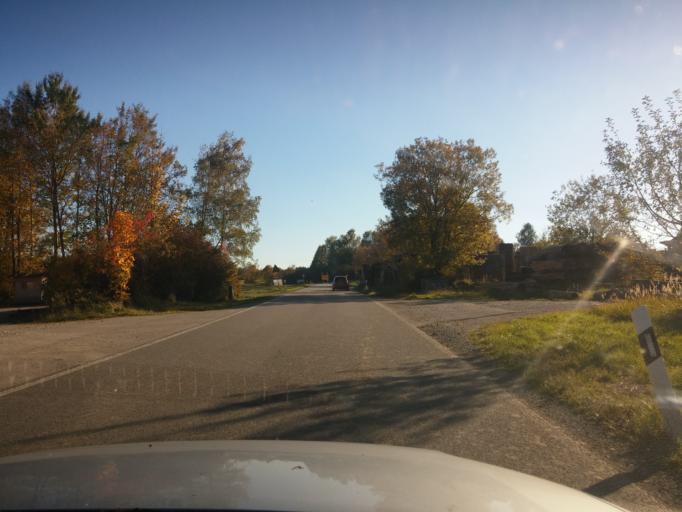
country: DE
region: Bavaria
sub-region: Upper Bavaria
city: Egmating
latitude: 48.0062
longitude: 11.7999
